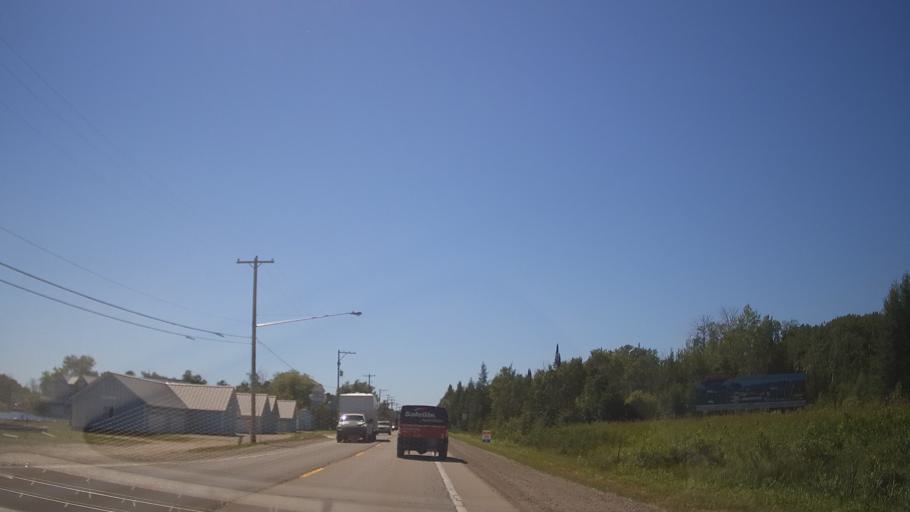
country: US
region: Michigan
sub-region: Emmet County
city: Petoskey
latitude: 45.4239
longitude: -84.8392
